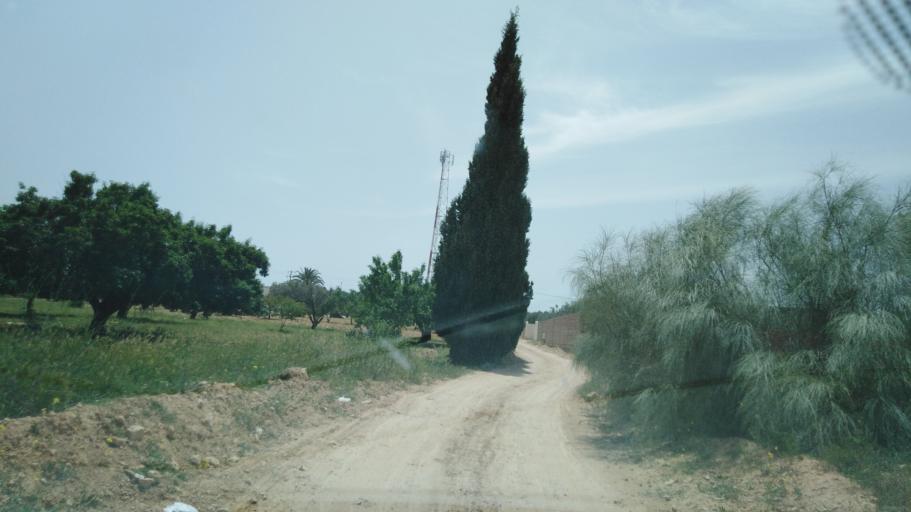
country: TN
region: Safaqis
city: Sfax
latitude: 34.7322
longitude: 10.5562
